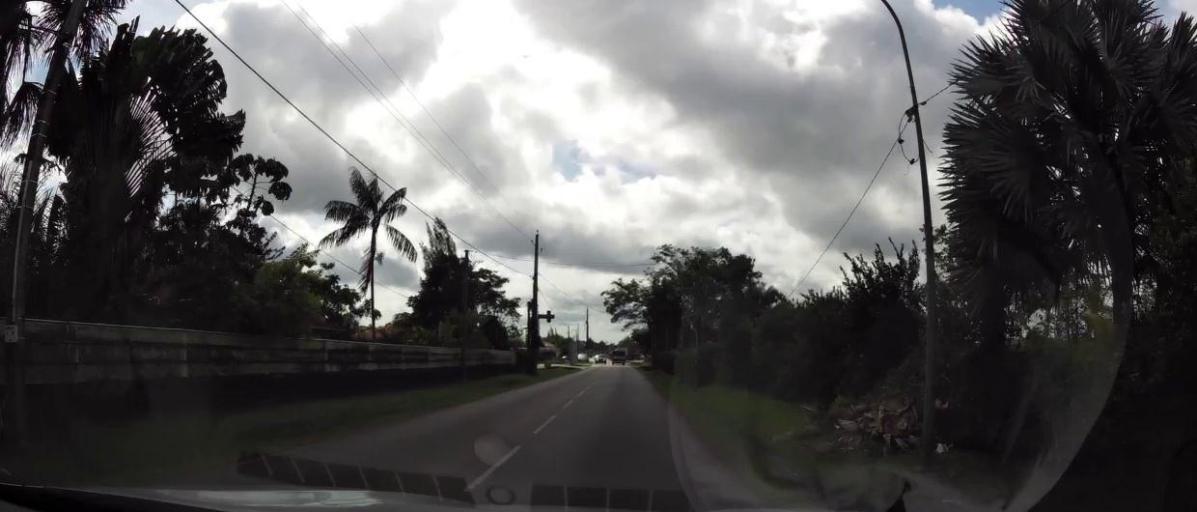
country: GF
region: Guyane
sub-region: Guyane
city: Matoury
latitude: 4.8750
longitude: -52.3329
